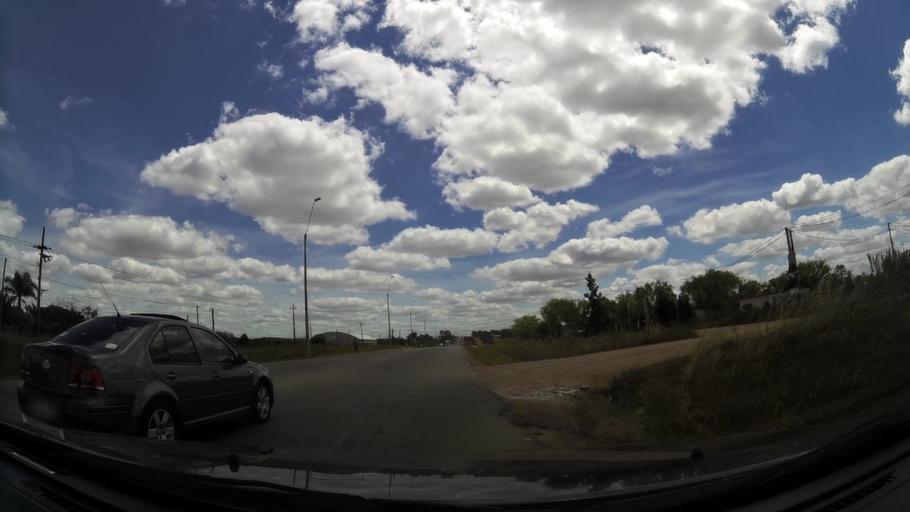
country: UY
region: Canelones
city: Colonia Nicolich
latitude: -34.7958
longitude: -56.0031
